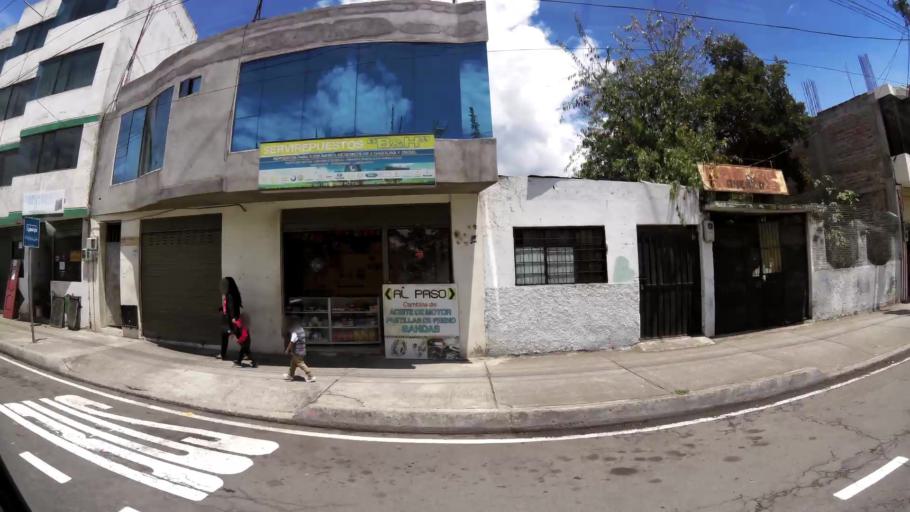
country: EC
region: Tungurahua
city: Ambato
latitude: -1.2634
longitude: -78.6125
